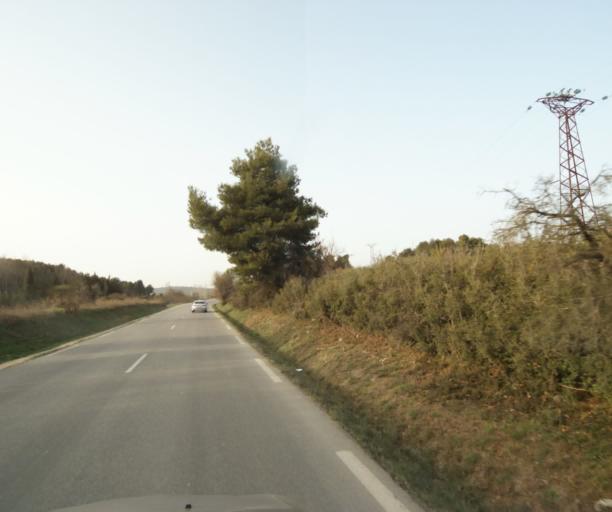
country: FR
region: Provence-Alpes-Cote d'Azur
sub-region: Departement des Bouches-du-Rhone
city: Eguilles
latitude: 43.5330
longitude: 5.3497
